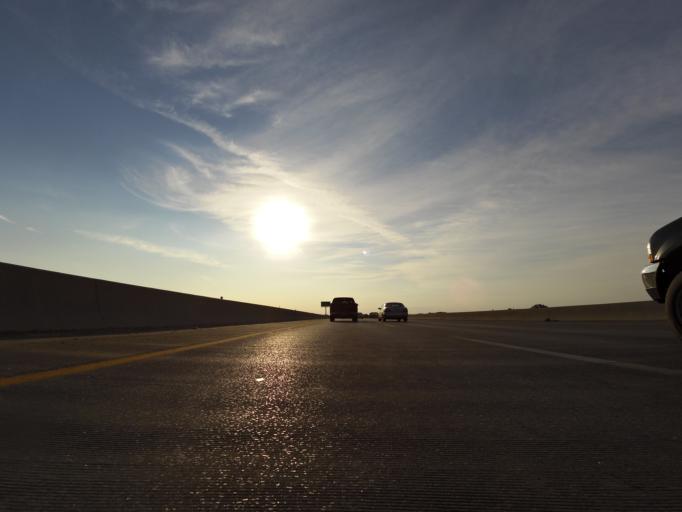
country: US
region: Kansas
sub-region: Sedgwick County
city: Bellaire
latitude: 37.7435
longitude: -97.2951
